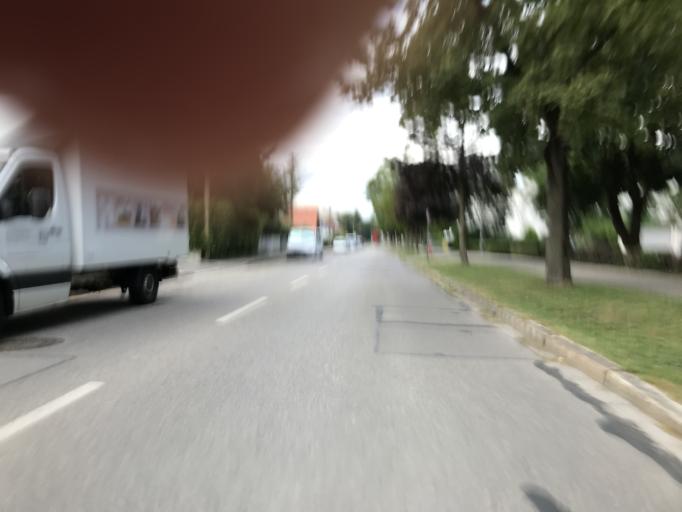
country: DE
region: Bavaria
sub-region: Upper Bavaria
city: Puchheim
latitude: 48.1764
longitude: 11.3535
